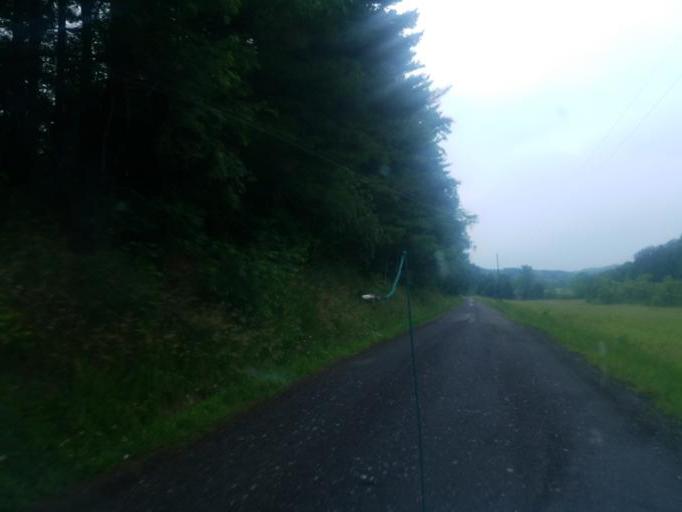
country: US
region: Ohio
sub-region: Columbiana County
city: Salineville
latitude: 40.5828
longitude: -80.9322
